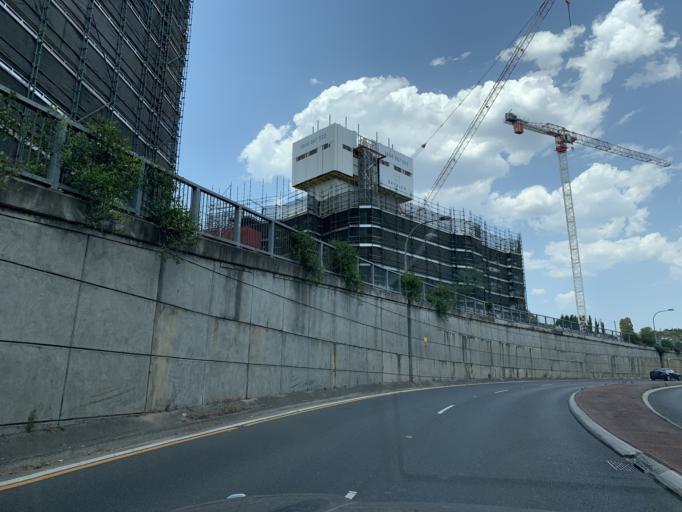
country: AU
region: New South Wales
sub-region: The Hills Shire
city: Castle Hill
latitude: -33.7283
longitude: 151.0071
